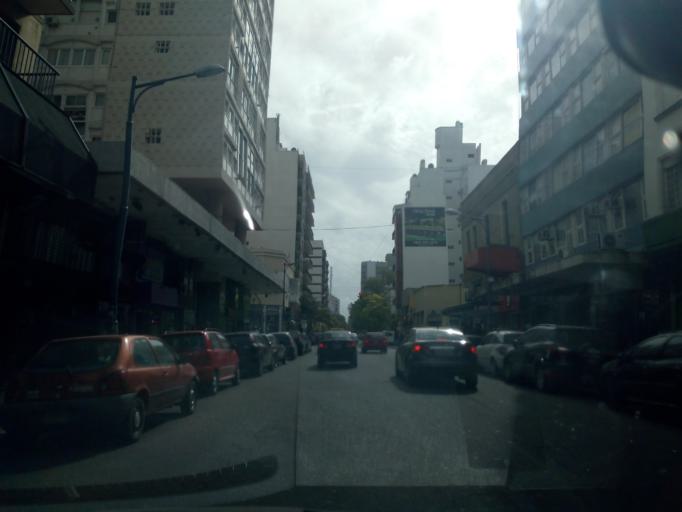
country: AR
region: Buenos Aires
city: Mar del Plata
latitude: -38.0001
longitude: -57.5480
